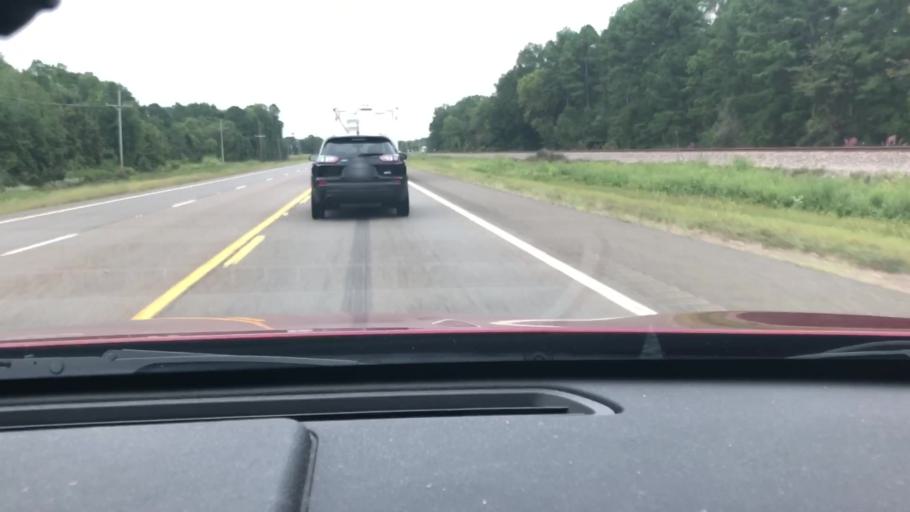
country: US
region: Arkansas
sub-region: Lafayette County
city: Lewisville
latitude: 33.3571
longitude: -93.5959
